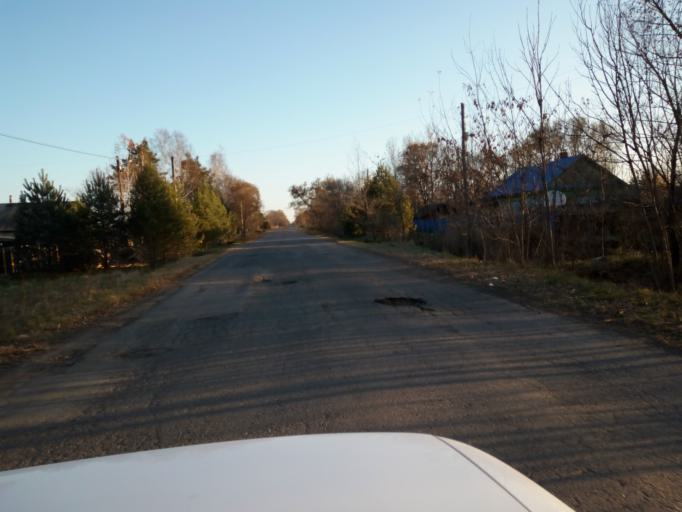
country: RU
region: Primorskiy
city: Lazo
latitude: 45.8663
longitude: 133.6437
